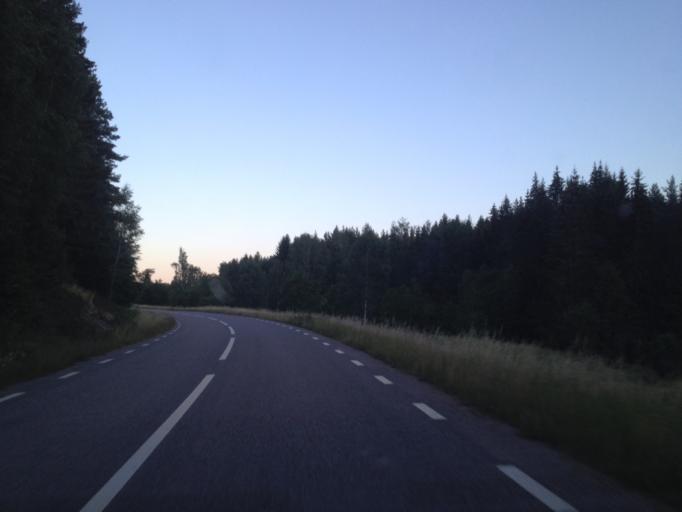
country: SE
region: Kalmar
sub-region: Vasterviks Kommun
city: Overum
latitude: 58.0048
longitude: 16.1734
